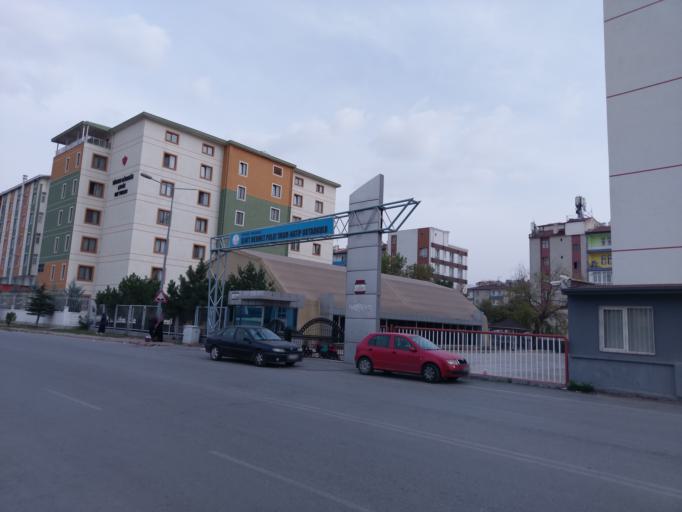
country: TR
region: Kayseri
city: Kayseri
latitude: 38.7117
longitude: 35.4886
